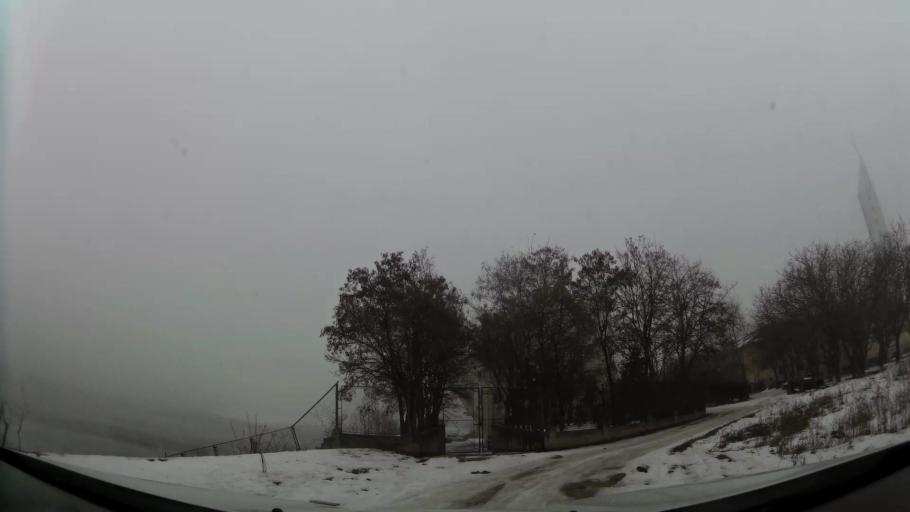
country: RO
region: Ilfov
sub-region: Comuna Chiajna
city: Rosu
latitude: 44.4470
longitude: 26.0355
